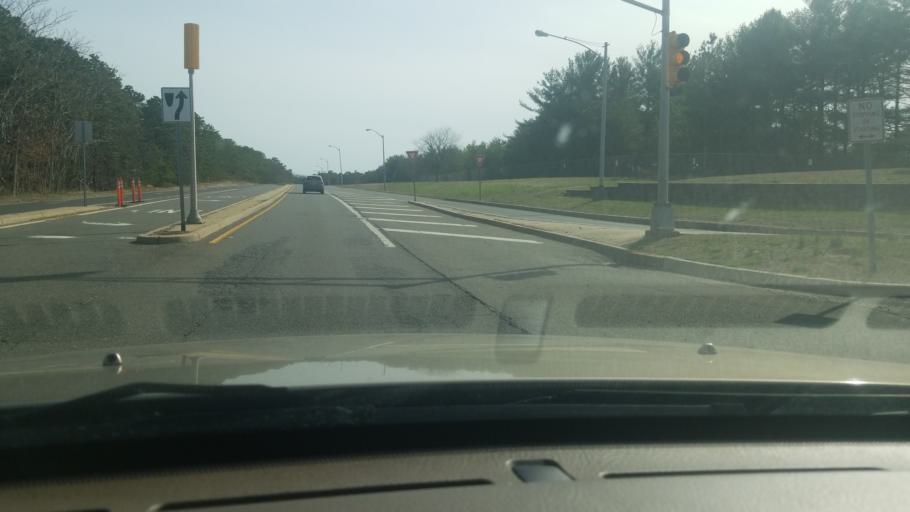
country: US
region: New Jersey
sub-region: Ocean County
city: Lakehurst
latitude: 40.0262
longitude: -74.3081
